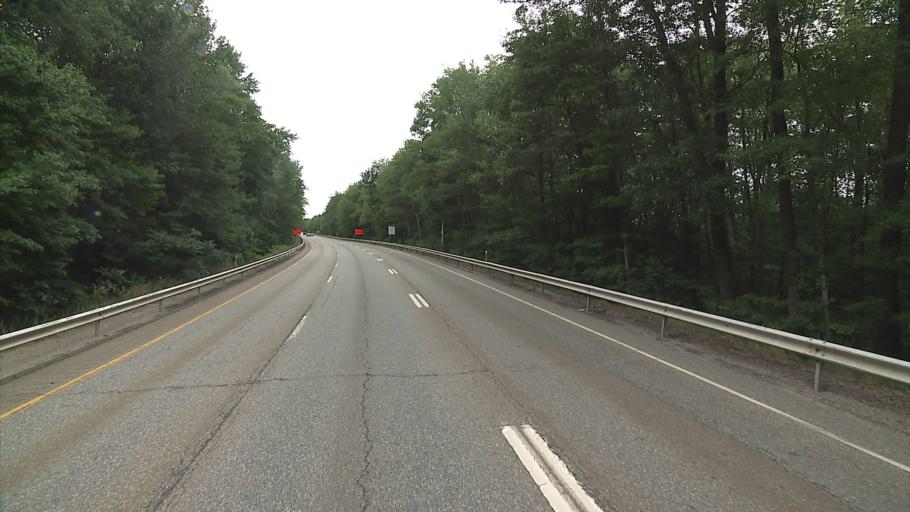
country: US
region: Connecticut
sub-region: Litchfield County
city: Thomaston
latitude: 41.6959
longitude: -73.0682
